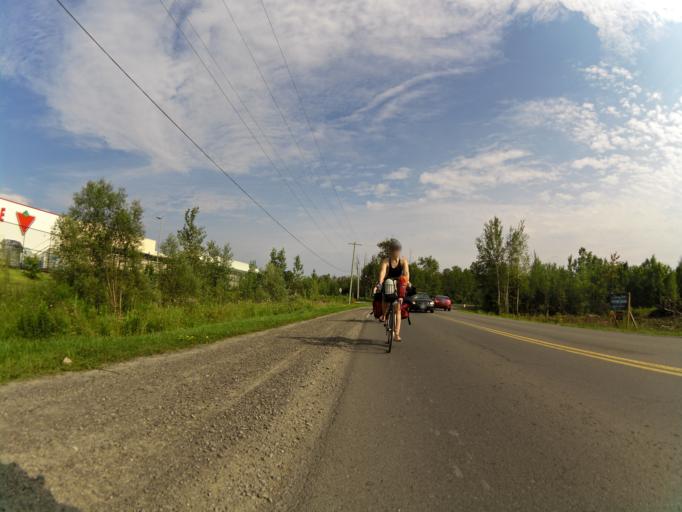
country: CA
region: Ontario
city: Prescott
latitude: 45.0280
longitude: -75.6347
